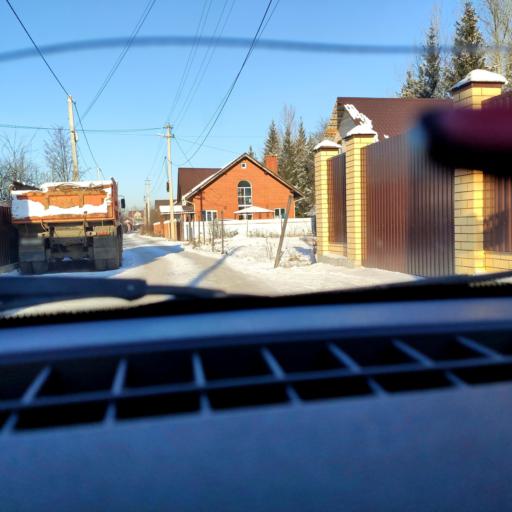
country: RU
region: Bashkortostan
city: Ufa
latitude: 54.6553
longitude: 55.9259
